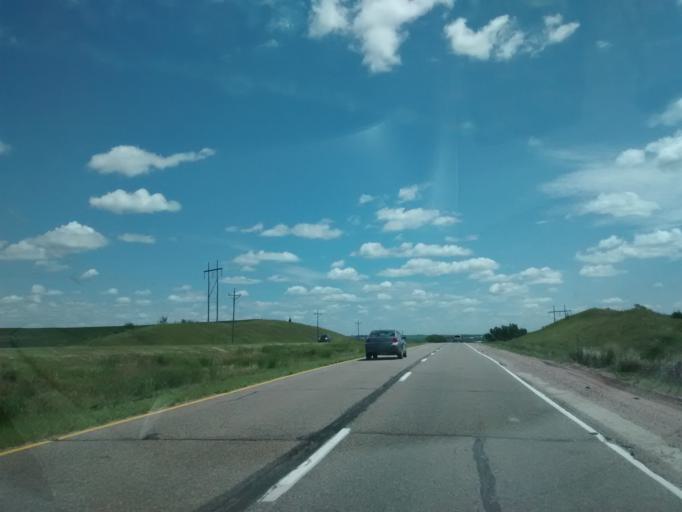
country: US
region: Iowa
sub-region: Woodbury County
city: Moville
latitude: 42.4747
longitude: -96.1132
